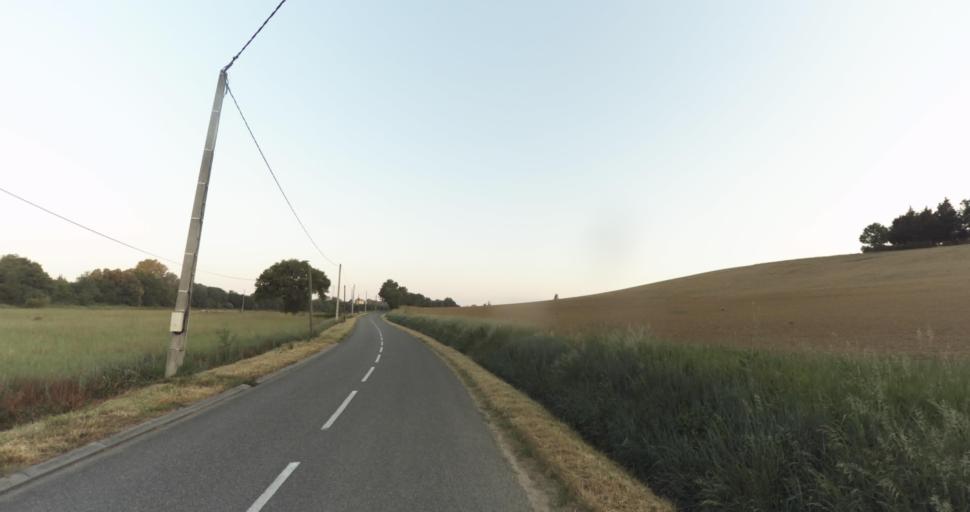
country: FR
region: Midi-Pyrenees
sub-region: Departement du Gers
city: Pujaudran
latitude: 43.6617
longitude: 1.1018
